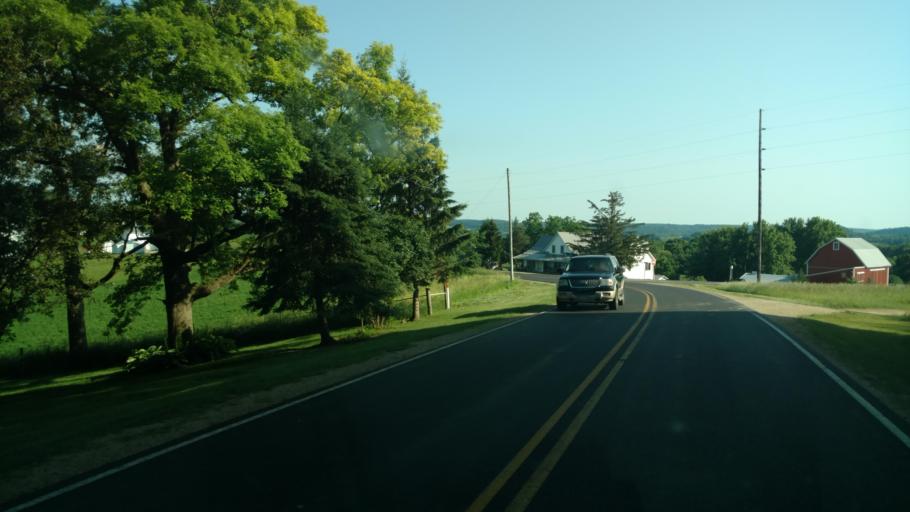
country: US
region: Wisconsin
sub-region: Vernon County
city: Hillsboro
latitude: 43.6690
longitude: -90.3516
